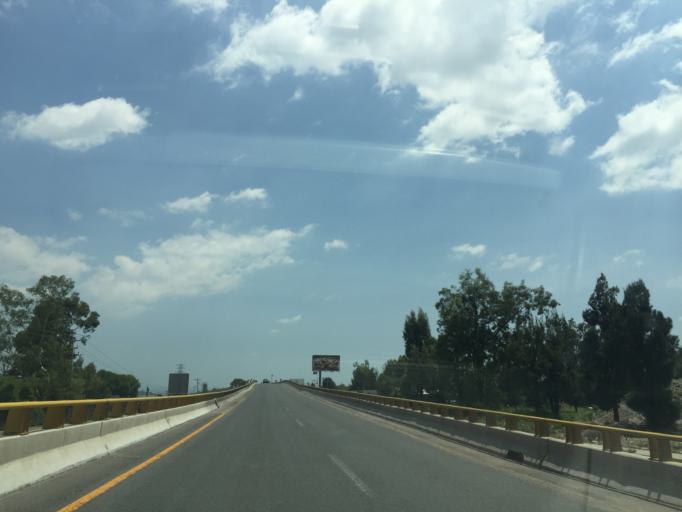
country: MX
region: Guanajuato
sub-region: Leon
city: Fraccionamiento Paseo de las Torres
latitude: 21.1806
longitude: -101.7425
